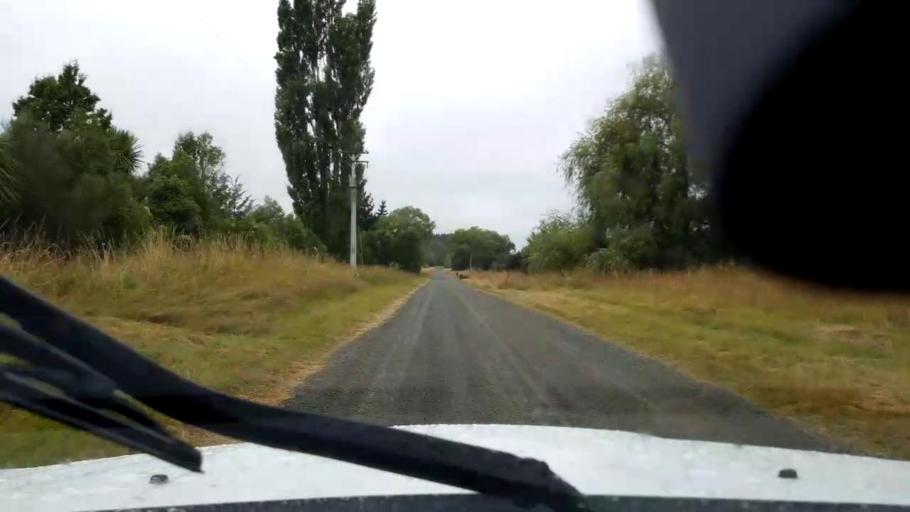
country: NZ
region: Canterbury
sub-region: Timaru District
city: Pleasant Point
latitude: -44.2513
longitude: 171.2631
